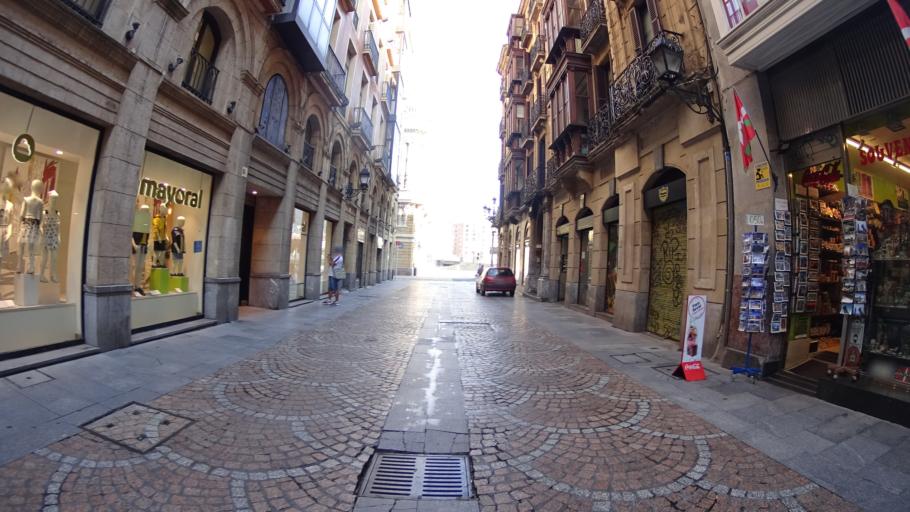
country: ES
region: Basque Country
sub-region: Bizkaia
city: Bilbao
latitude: 43.2589
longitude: -2.9245
